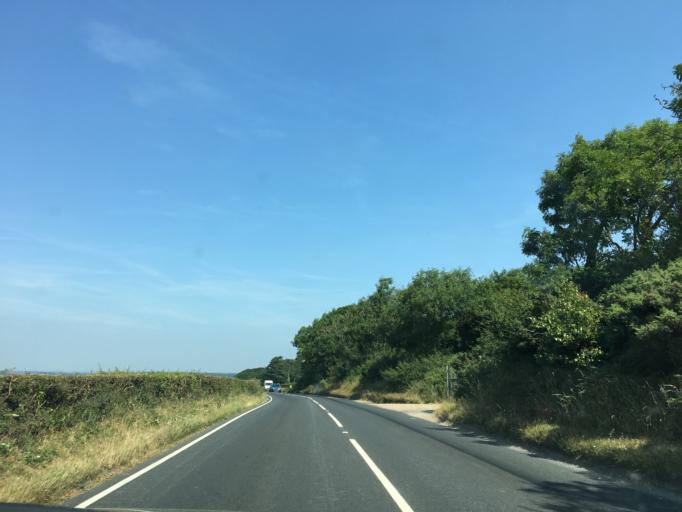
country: GB
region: England
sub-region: Isle of Wight
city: Newchurch
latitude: 50.6977
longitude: -1.2408
